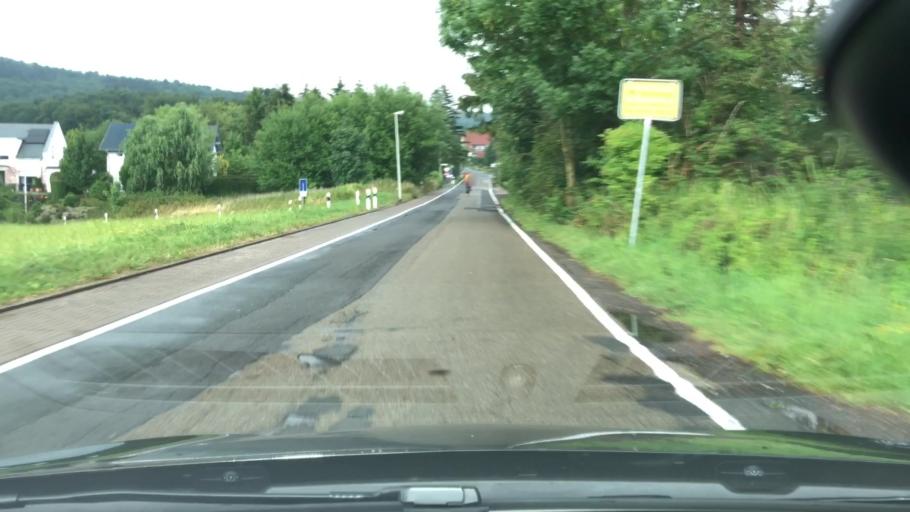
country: DE
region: North Rhine-Westphalia
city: Porta Westfalica
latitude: 52.2333
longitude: 8.9425
